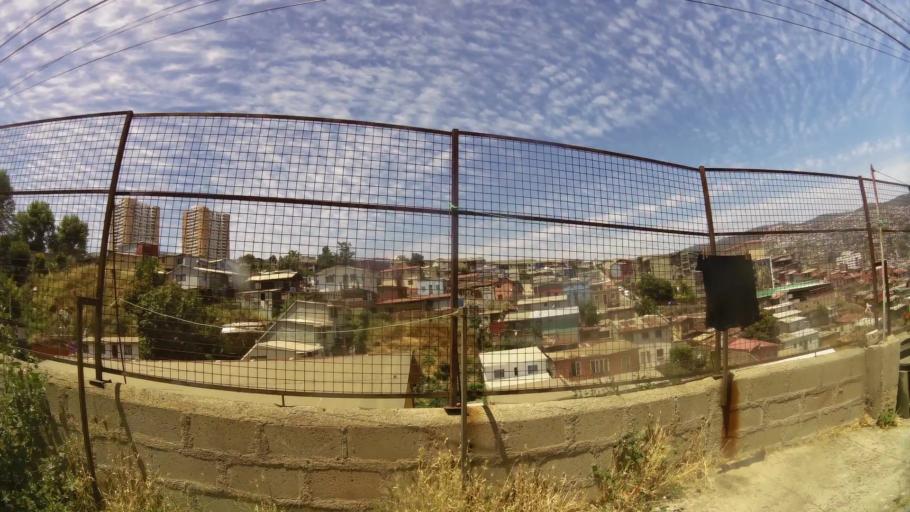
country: CL
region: Valparaiso
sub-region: Provincia de Valparaiso
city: Valparaiso
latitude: -33.0444
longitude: -71.6004
